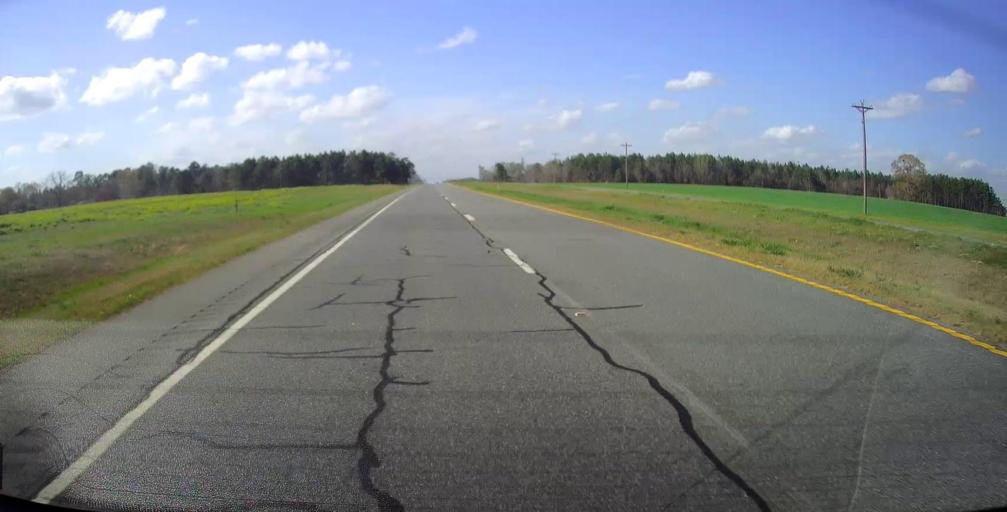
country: US
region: Georgia
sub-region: Pulaski County
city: Hawkinsville
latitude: 32.2227
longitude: -83.3565
